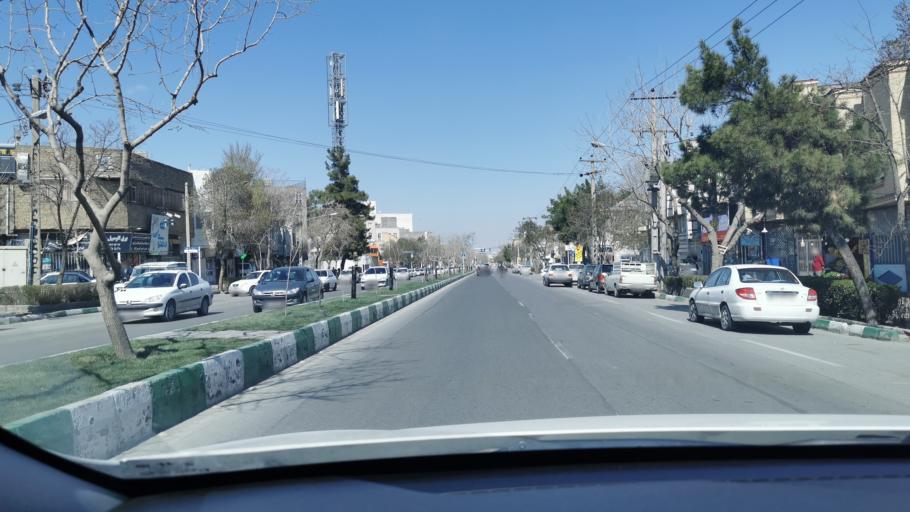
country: IR
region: Razavi Khorasan
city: Mashhad
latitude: 36.2747
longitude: 59.5762
